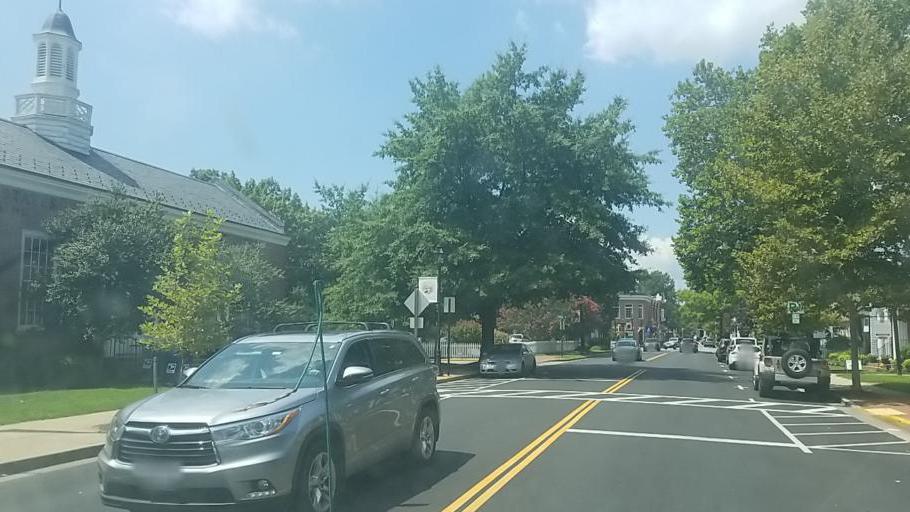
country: US
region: Maryland
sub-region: Talbot County
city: Easton
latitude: 38.7741
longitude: -76.0733
